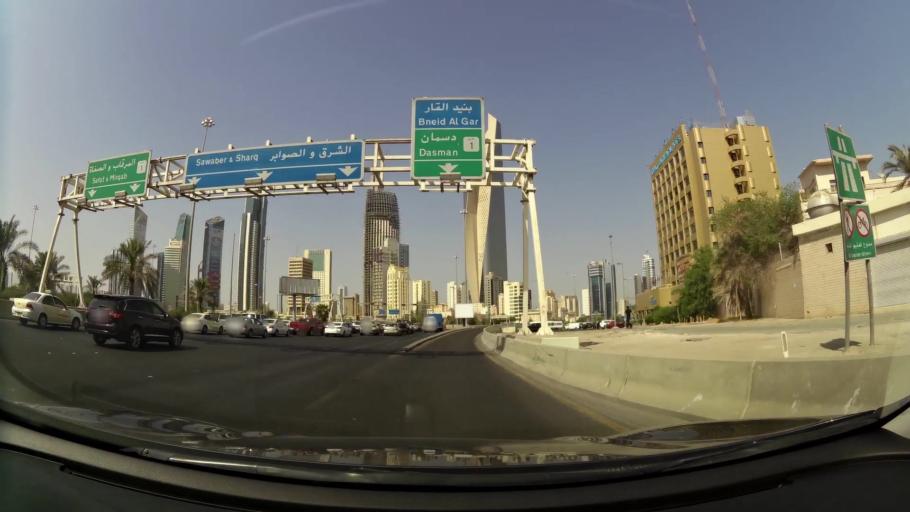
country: KW
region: Al Asimah
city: Ad Dasmah
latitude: 29.3733
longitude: 47.9978
